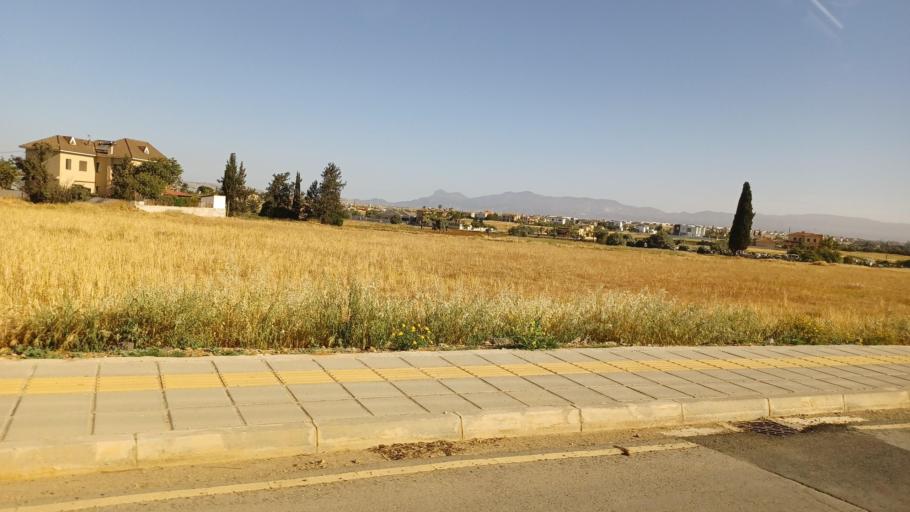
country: CY
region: Lefkosia
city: Kokkinotrimithia
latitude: 35.1495
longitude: 33.1913
